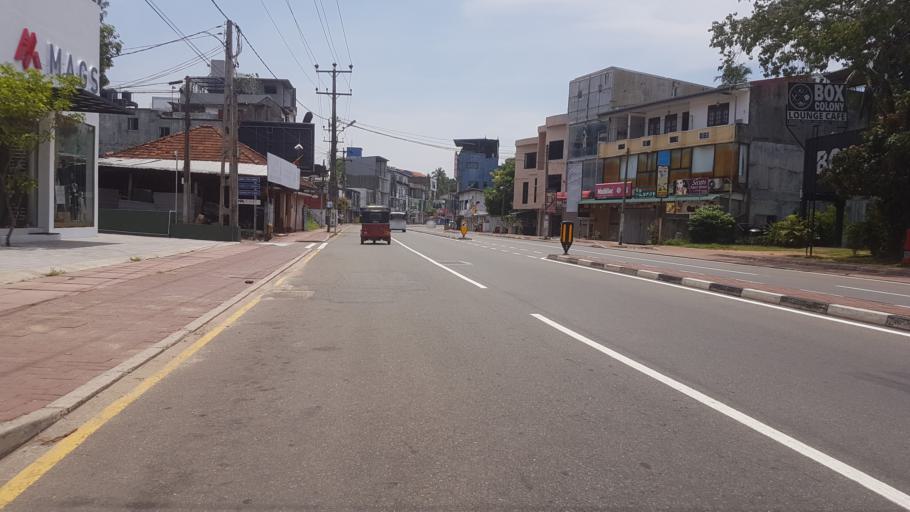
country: LK
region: Western
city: Battaramulla South
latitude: 6.8934
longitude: 79.9263
